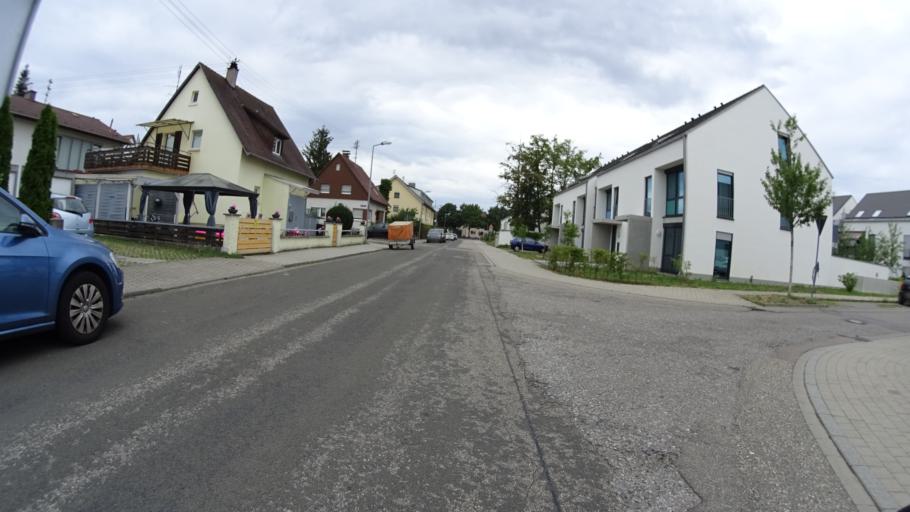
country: DE
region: Baden-Wuerttemberg
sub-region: Karlsruhe Region
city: Karlsruhe
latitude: 49.0361
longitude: 8.3436
